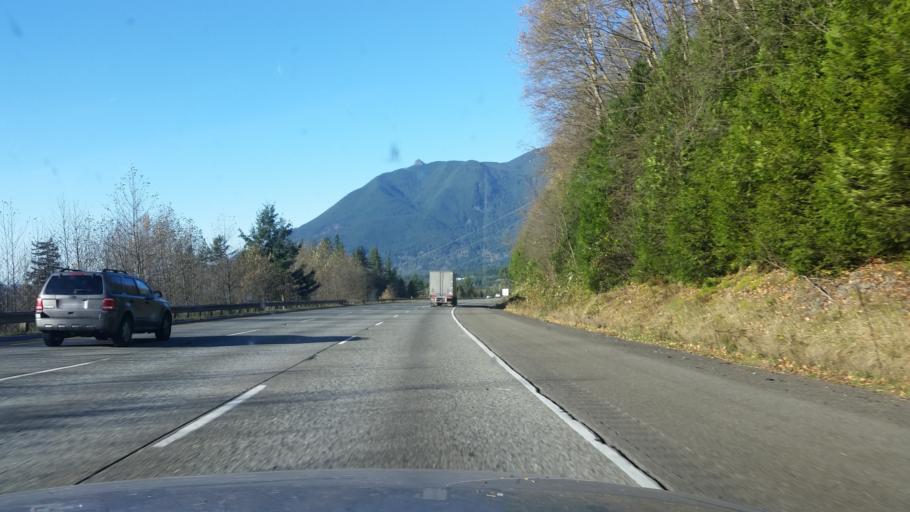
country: US
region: Washington
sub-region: King County
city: Tanner
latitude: 47.4501
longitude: -121.6994
